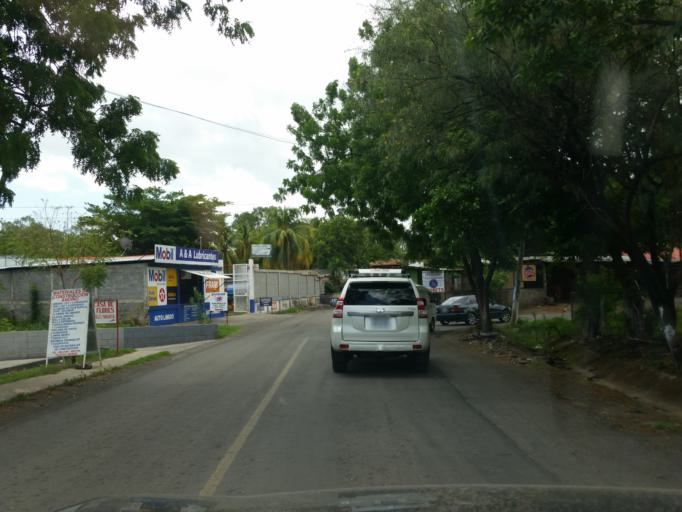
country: NI
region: Managua
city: Managua
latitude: 12.1269
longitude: -86.2439
